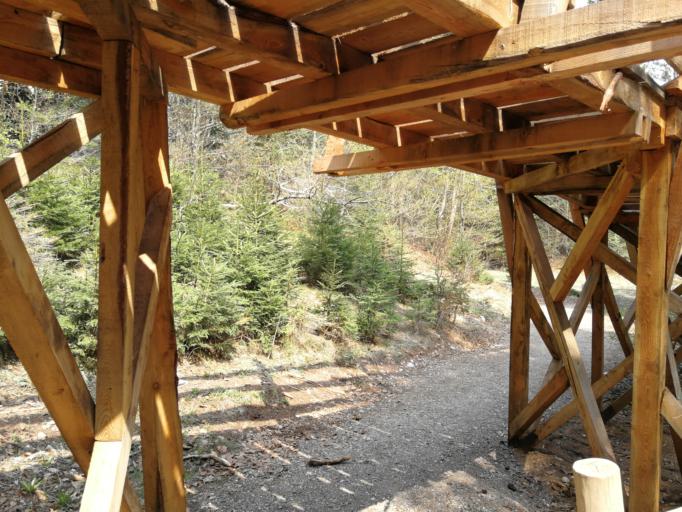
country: IT
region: Trentino-Alto Adige
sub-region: Provincia di Trento
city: Molveno
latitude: 46.1535
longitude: 10.9665
